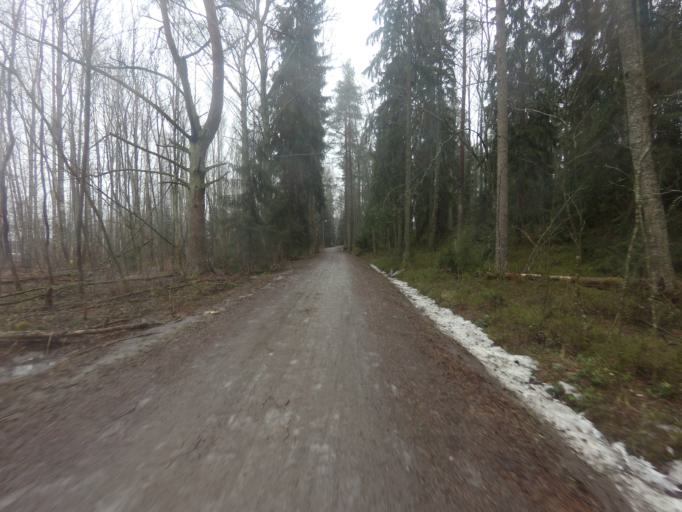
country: FI
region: Uusimaa
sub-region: Helsinki
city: Espoo
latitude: 60.1558
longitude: 24.6930
